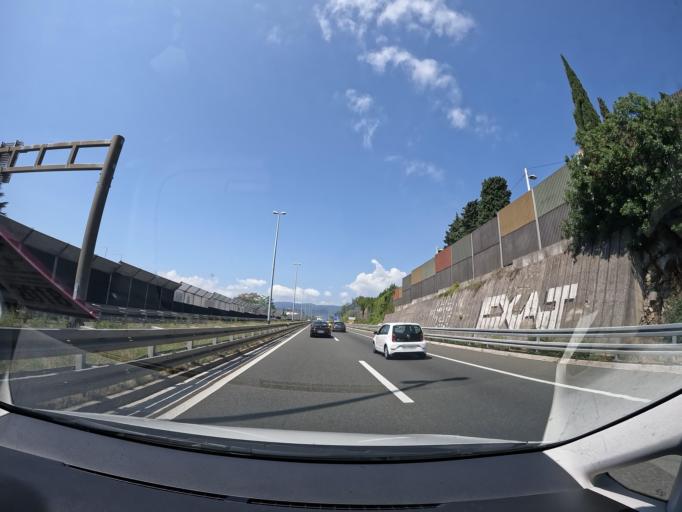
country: SI
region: Ilirska Bistrica
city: Ilirska Bistrica
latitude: 45.5376
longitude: 14.3844
